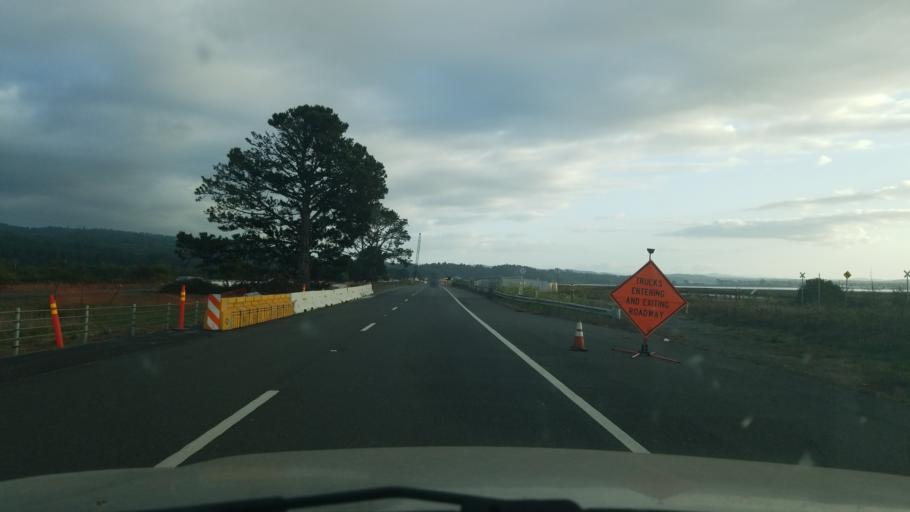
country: US
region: California
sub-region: Humboldt County
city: Arcata
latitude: 40.8479
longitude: -124.0821
